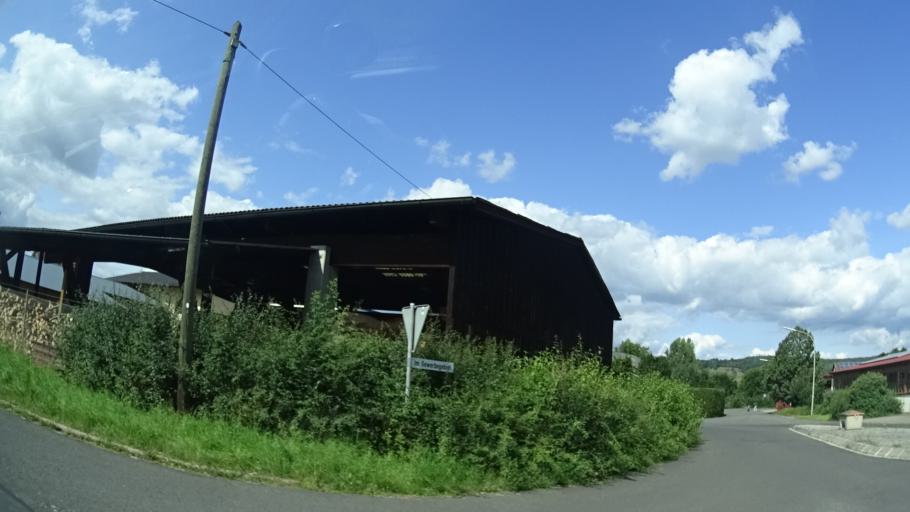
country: DE
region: Bavaria
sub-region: Regierungsbezirk Unterfranken
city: Eltmann
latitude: 49.9785
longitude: 10.6415
